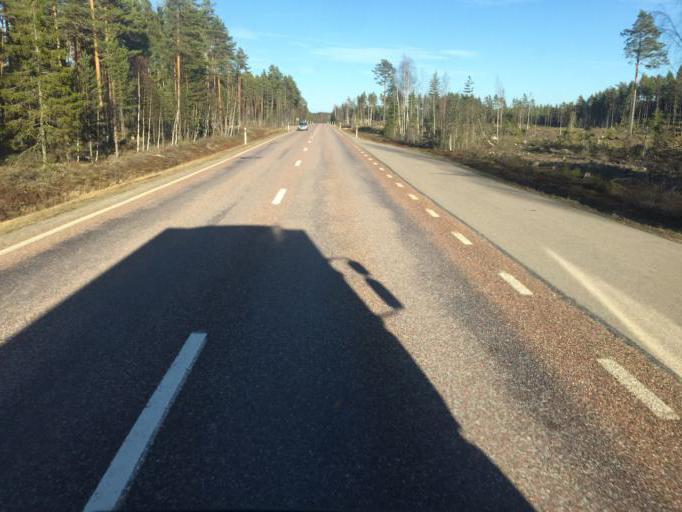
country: SE
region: Dalarna
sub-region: Vansbro Kommun
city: Jarna
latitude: 60.4714
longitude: 14.6277
